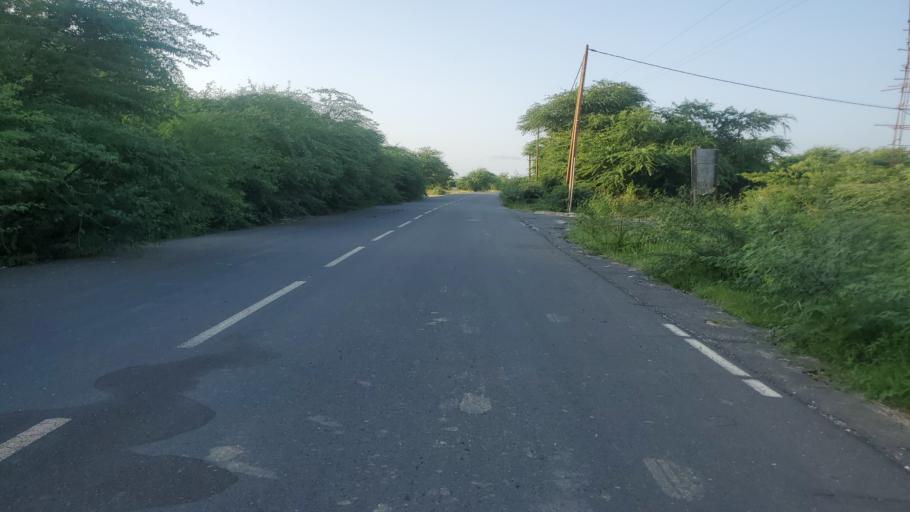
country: SN
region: Saint-Louis
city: Saint-Louis
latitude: 16.2073
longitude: -16.4153
